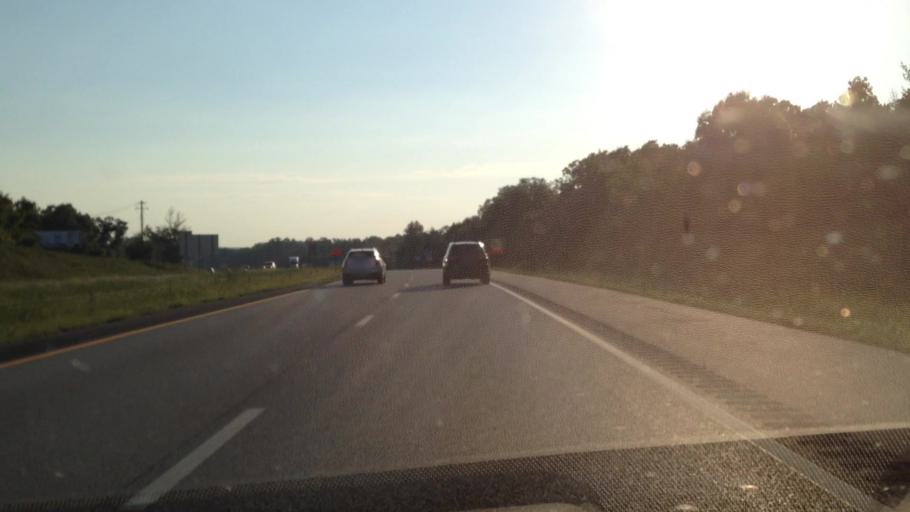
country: US
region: Missouri
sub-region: Jasper County
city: Joplin
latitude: 37.0452
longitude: -94.4994
